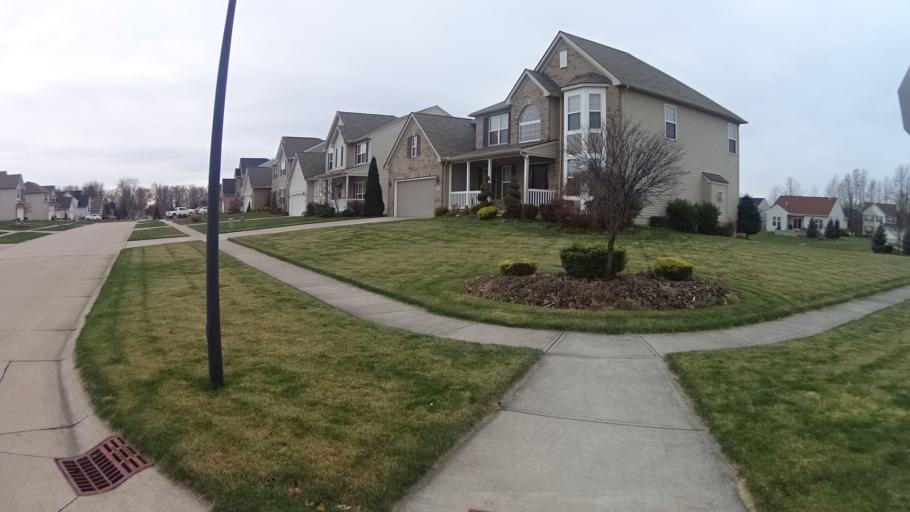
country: US
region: Ohio
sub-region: Lorain County
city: North Ridgeville
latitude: 41.3734
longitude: -81.9860
